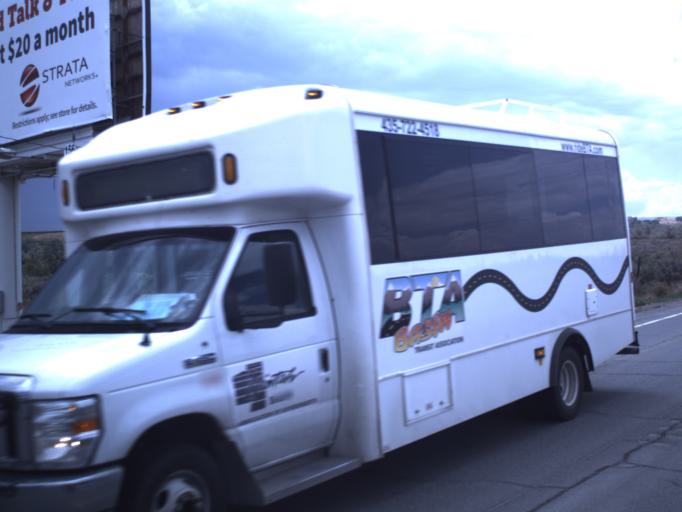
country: US
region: Utah
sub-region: Duchesne County
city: Roosevelt
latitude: 40.1911
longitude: -110.0811
